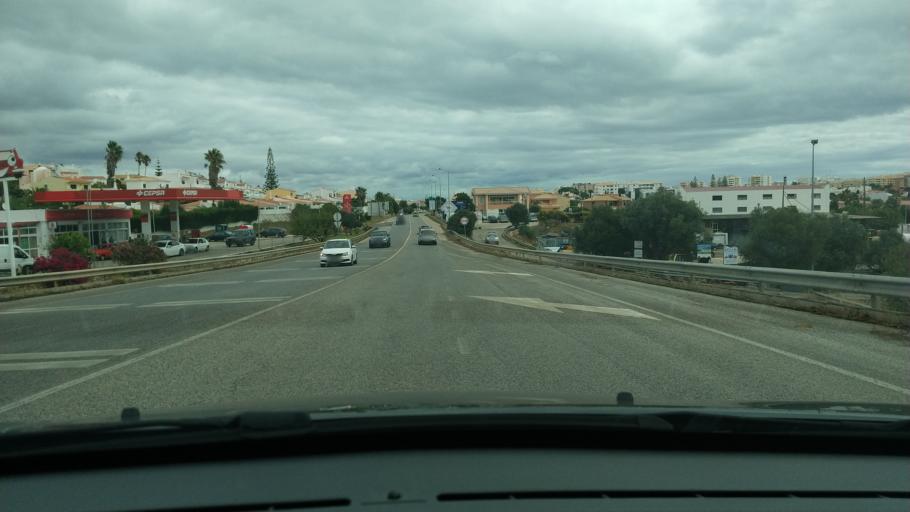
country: PT
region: Faro
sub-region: Lagos
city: Lagos
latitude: 37.1016
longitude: -8.6937
